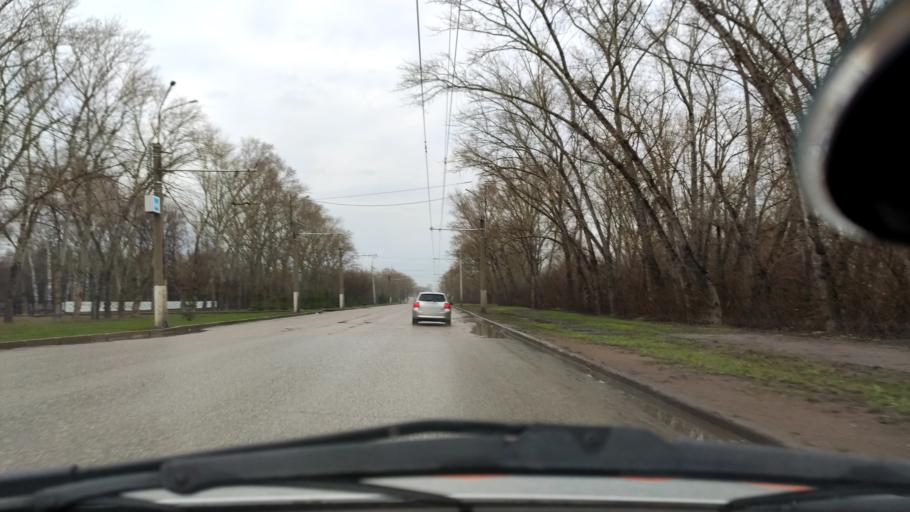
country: RU
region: Bashkortostan
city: Sterlitamak
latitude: 53.6576
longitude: 55.9488
